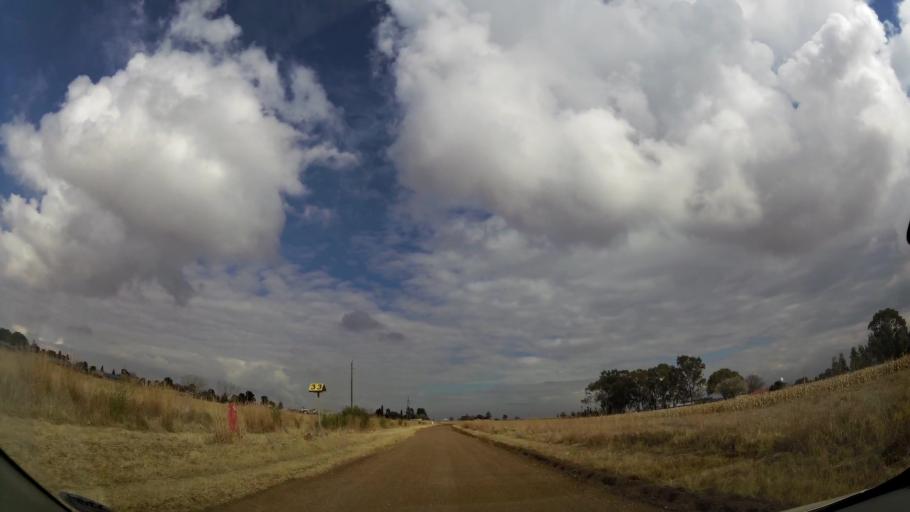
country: ZA
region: Gauteng
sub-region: Sedibeng District Municipality
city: Meyerton
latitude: -26.6045
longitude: 28.0779
